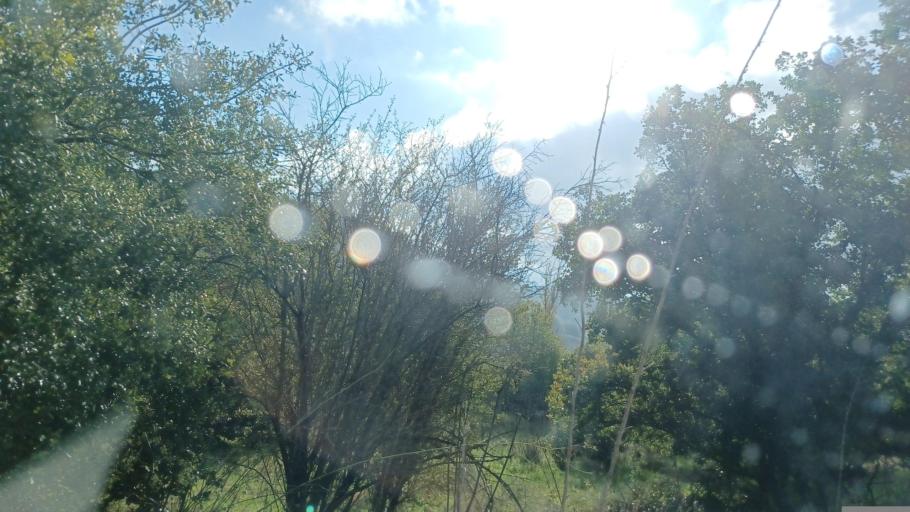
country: CY
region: Pafos
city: Mesogi
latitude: 34.8410
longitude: 32.5420
